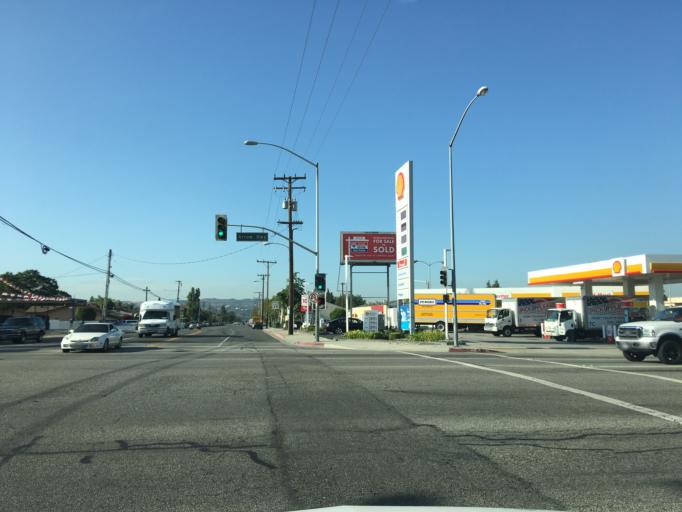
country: US
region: California
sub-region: Los Angeles County
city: Charter Oak
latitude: 34.1069
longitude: -117.8465
